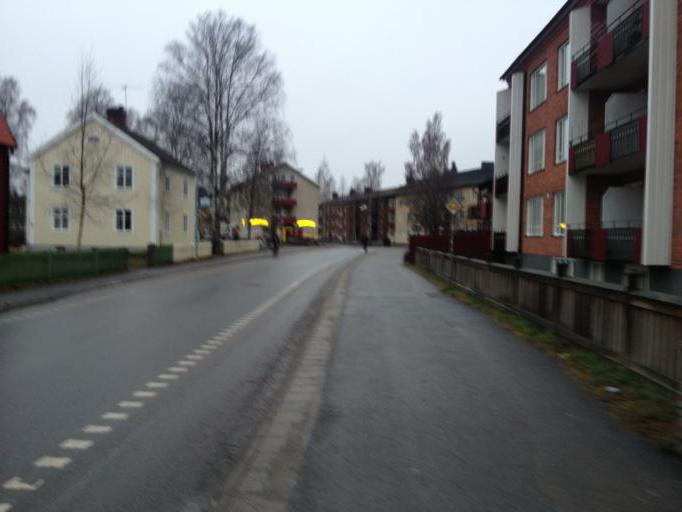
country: SE
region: Vaesterbotten
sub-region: Umea Kommun
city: Umea
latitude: 63.8216
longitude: 20.2857
